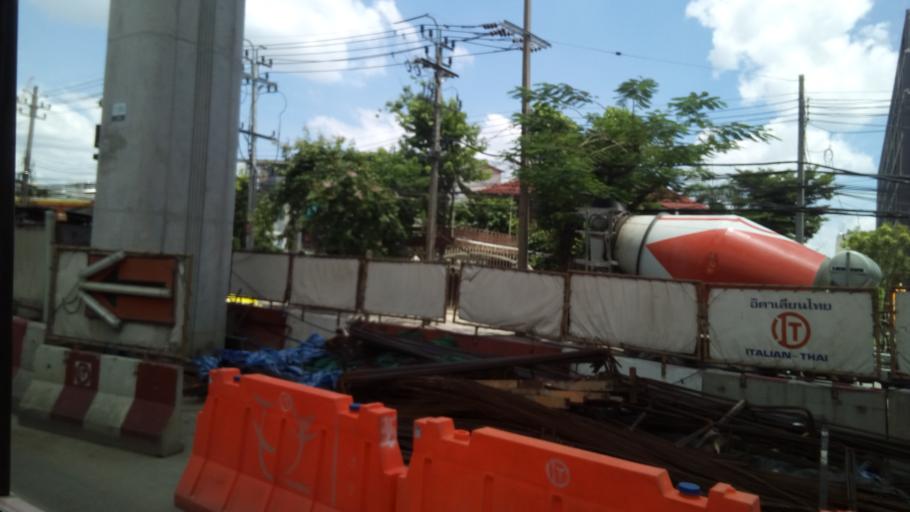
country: TH
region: Bangkok
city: Lak Si
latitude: 13.8819
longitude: 100.6007
